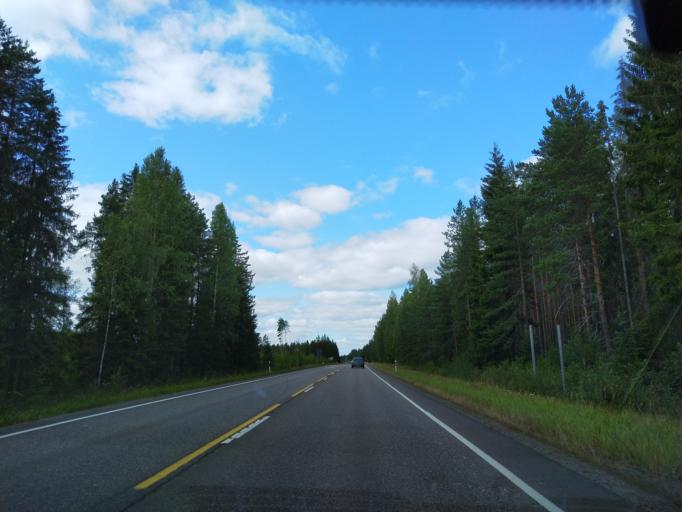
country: FI
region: Haeme
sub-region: Haemeenlinna
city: Renko
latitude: 60.7621
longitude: 24.2792
